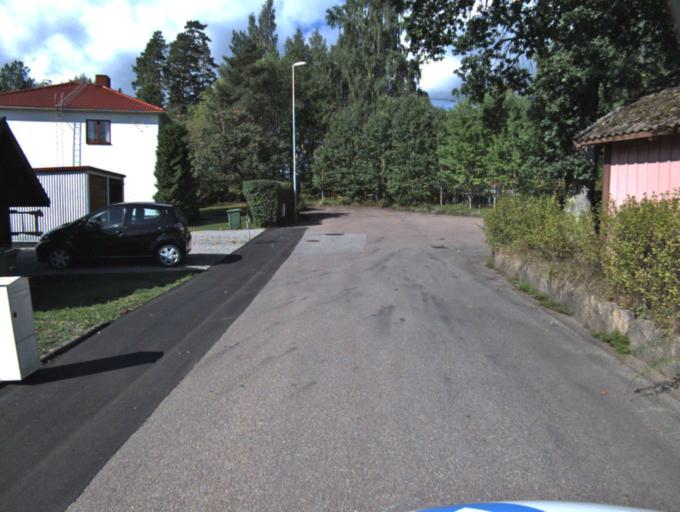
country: SE
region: Vaestra Goetaland
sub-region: Ulricehamns Kommun
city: Ulricehamn
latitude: 57.7998
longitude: 13.3936
